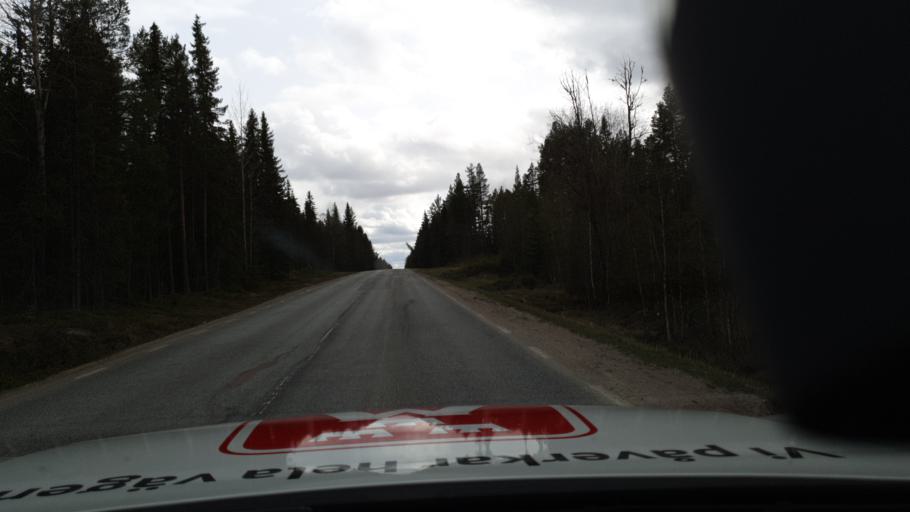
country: SE
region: Jaemtland
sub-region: Braecke Kommun
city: Braecke
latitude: 62.7793
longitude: 15.4640
